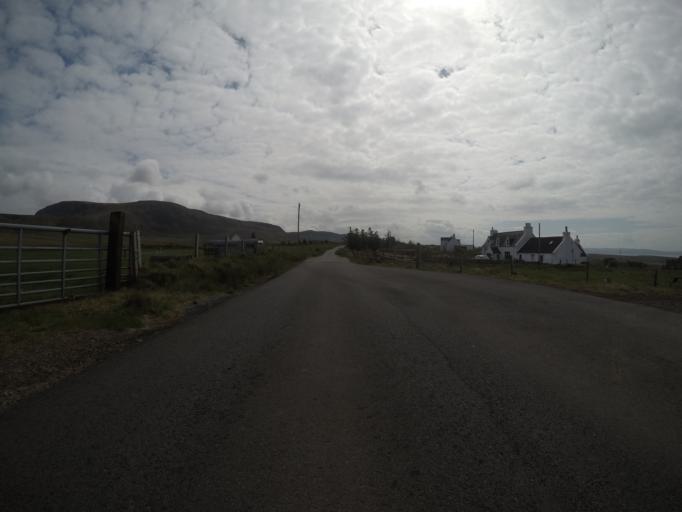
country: GB
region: Scotland
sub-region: Highland
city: Portree
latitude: 57.6434
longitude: -6.3775
